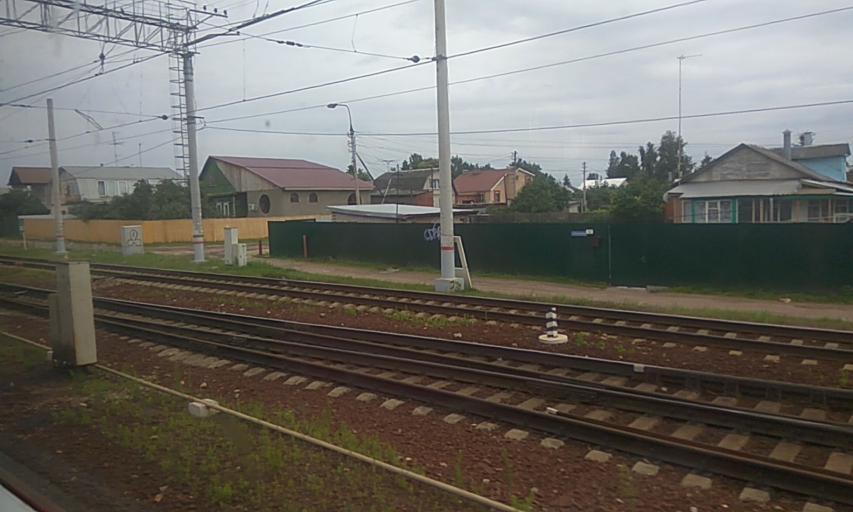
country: RU
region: Moskovskaya
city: Ramenskoye
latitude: 55.5623
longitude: 38.2338
